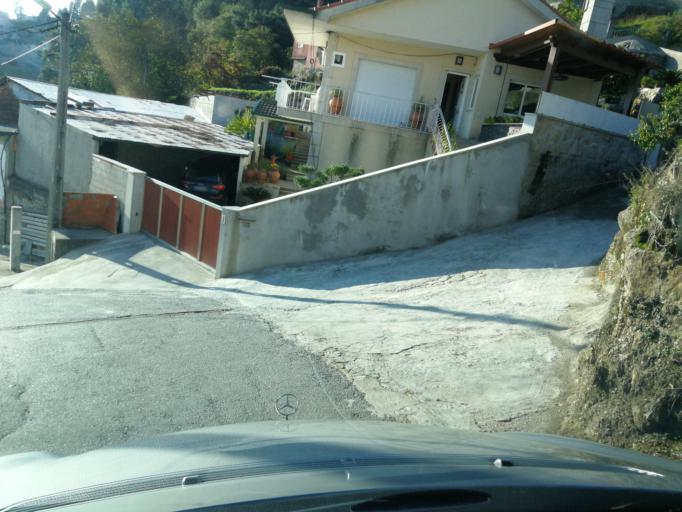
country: PT
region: Braga
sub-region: Braga
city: Oliveira
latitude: 41.4539
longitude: -8.4683
